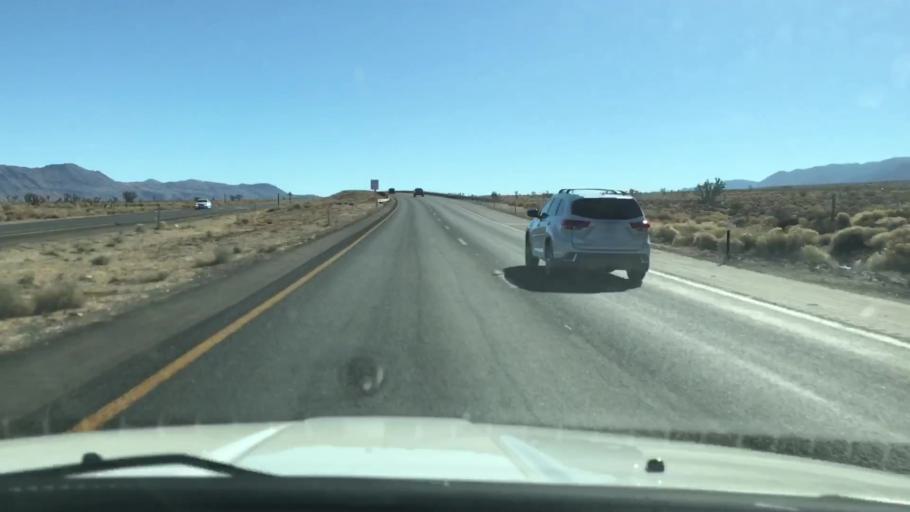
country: US
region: California
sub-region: Inyo County
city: Lone Pine
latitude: 36.2328
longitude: -117.9825
